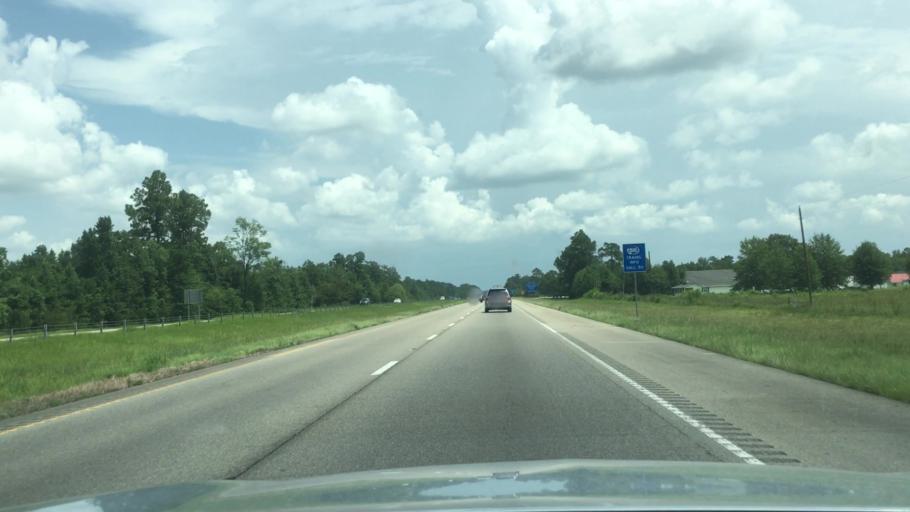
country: US
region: Mississippi
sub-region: Pearl River County
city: Nicholson
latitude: 30.4902
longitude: -89.6725
